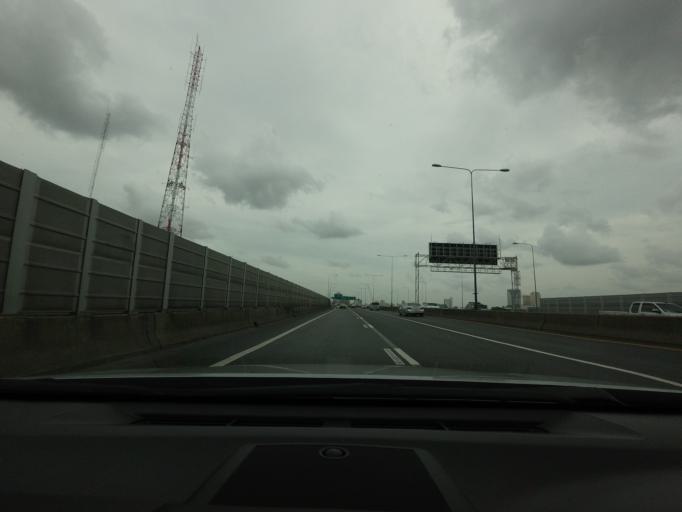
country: TH
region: Bangkok
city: Ratchathewi
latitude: 13.7621
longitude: 100.5263
